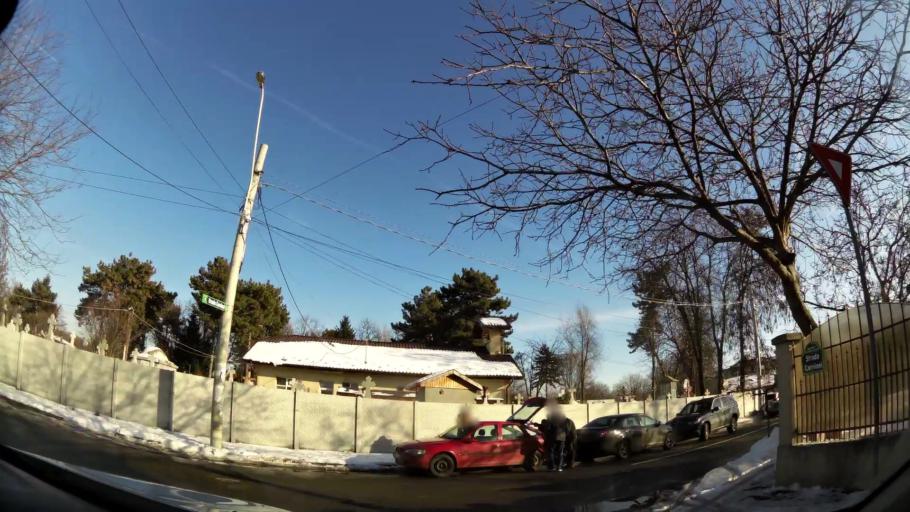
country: RO
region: Ilfov
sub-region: Voluntari City
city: Voluntari
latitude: 44.4810
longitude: 26.1536
